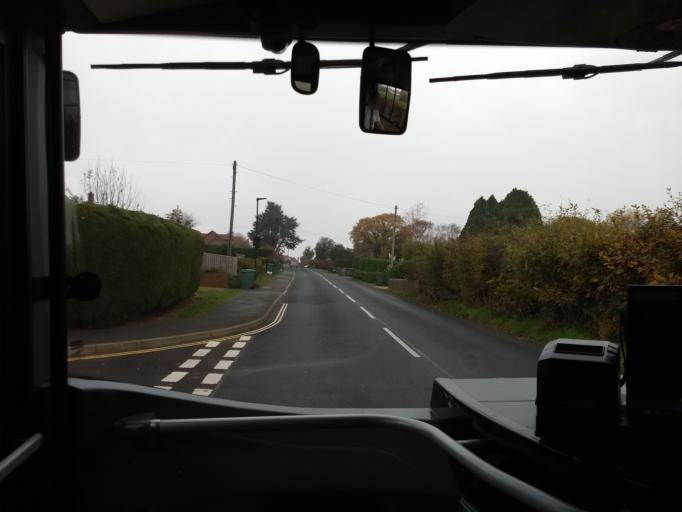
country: GB
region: England
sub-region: Isle of Wight
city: Newchurch
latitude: 50.6537
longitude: -1.2002
